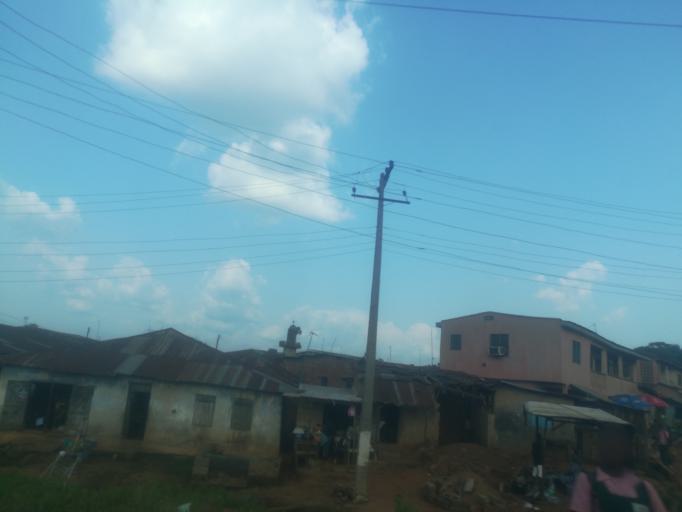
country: NG
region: Oyo
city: Moniya
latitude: 7.4878
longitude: 3.9144
